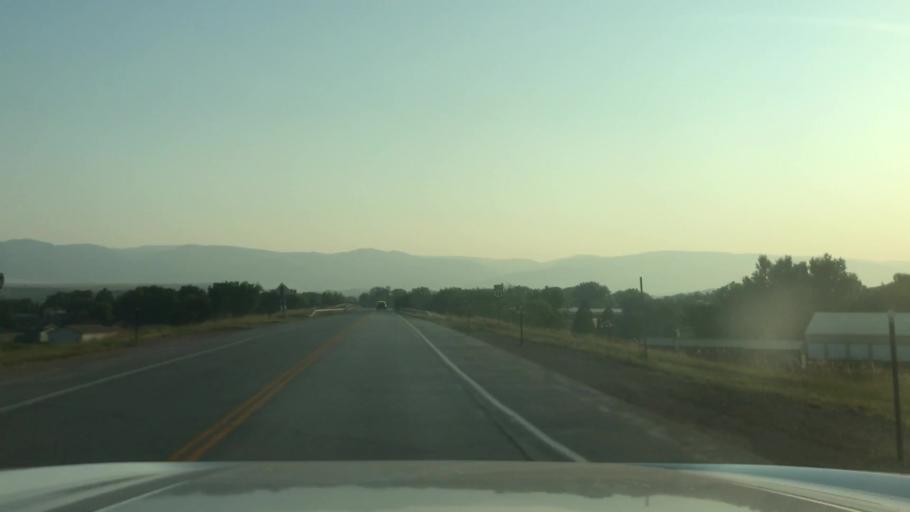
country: US
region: Wyoming
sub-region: Sheridan County
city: Sheridan
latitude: 44.9112
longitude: -107.1551
